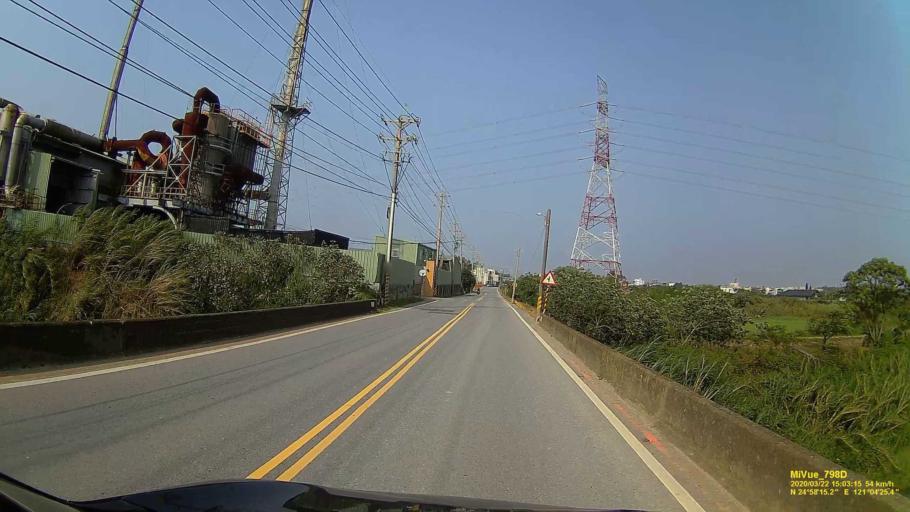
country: TW
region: Taiwan
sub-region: Hsinchu
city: Zhubei
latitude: 24.9712
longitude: 121.0740
